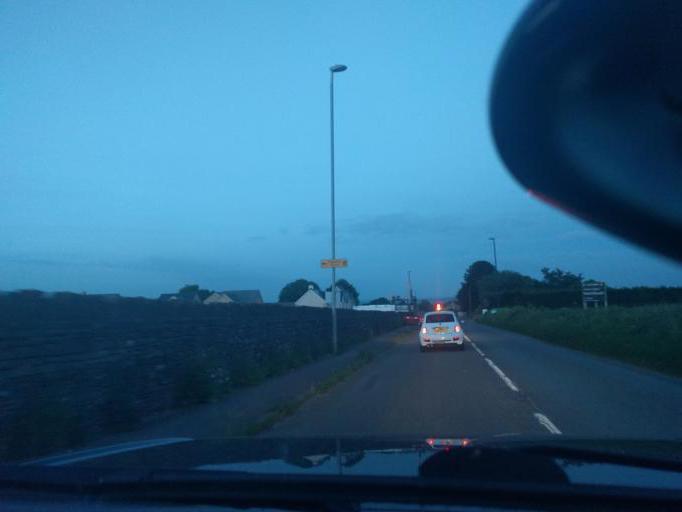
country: GB
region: England
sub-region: Wiltshire
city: Neston
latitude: 51.4321
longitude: -2.2184
